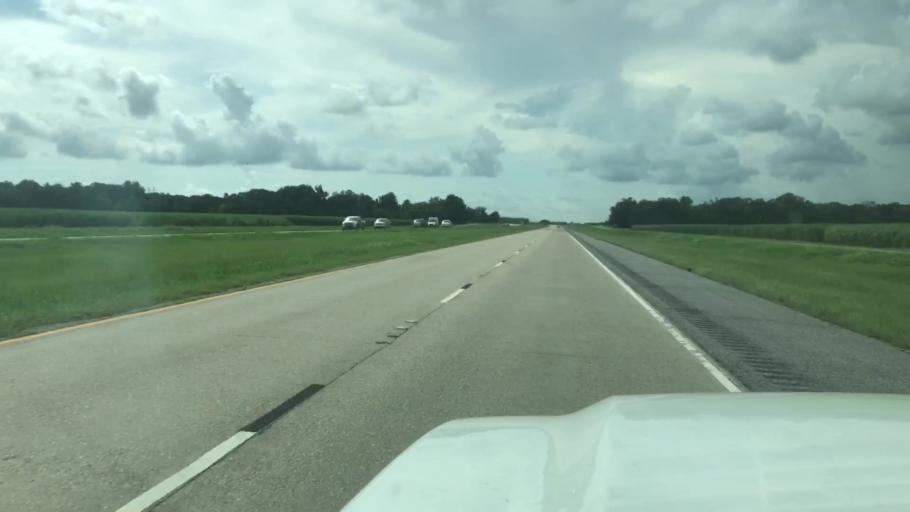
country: US
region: Louisiana
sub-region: Saint Mary Parish
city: Franklin
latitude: 29.7634
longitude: -91.4826
